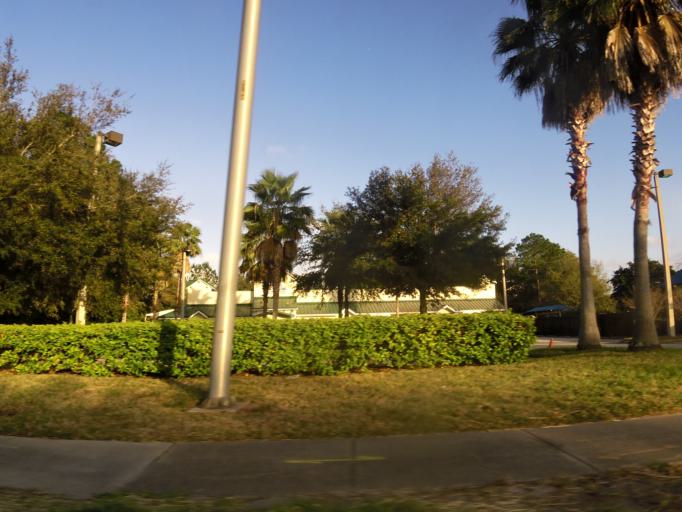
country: US
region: Florida
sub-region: Duval County
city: Jacksonville
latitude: 30.2663
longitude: -81.5548
